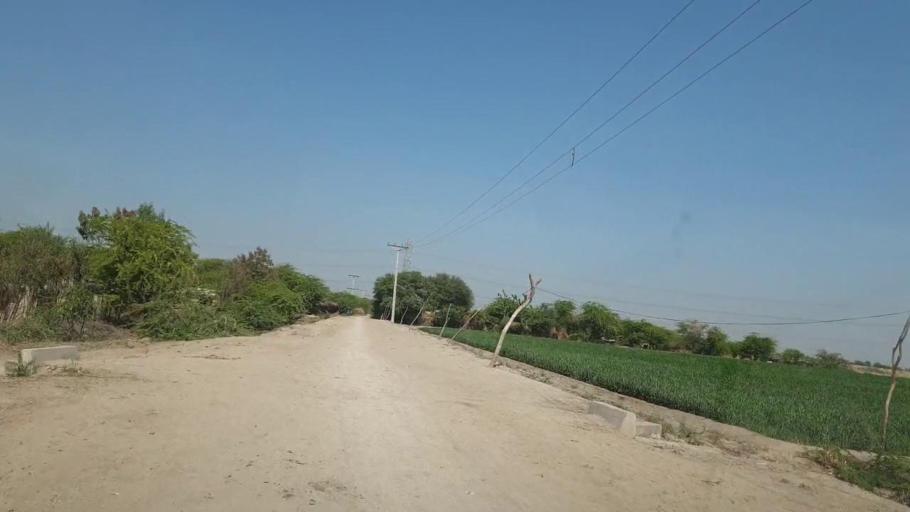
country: PK
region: Sindh
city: Kunri
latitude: 25.0998
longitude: 69.4573
